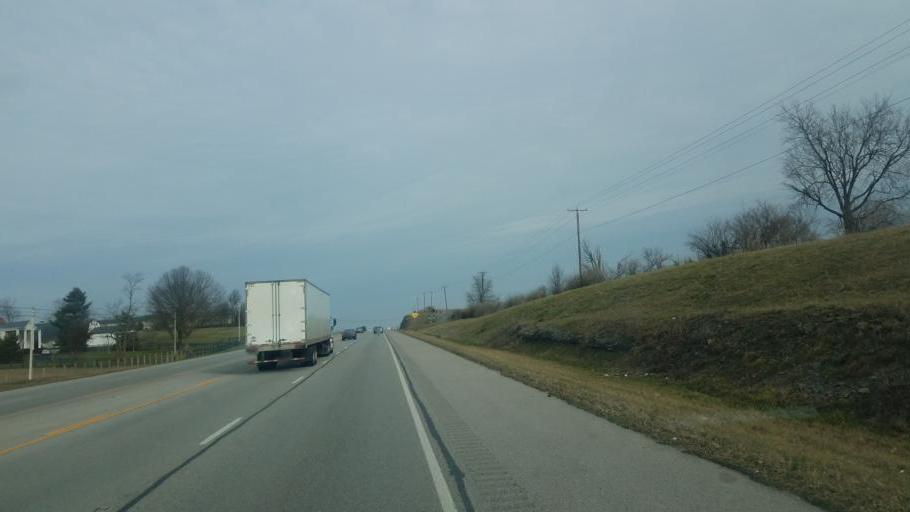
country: US
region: Kentucky
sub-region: Boyle County
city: Junction City
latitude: 37.6082
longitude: -84.7740
